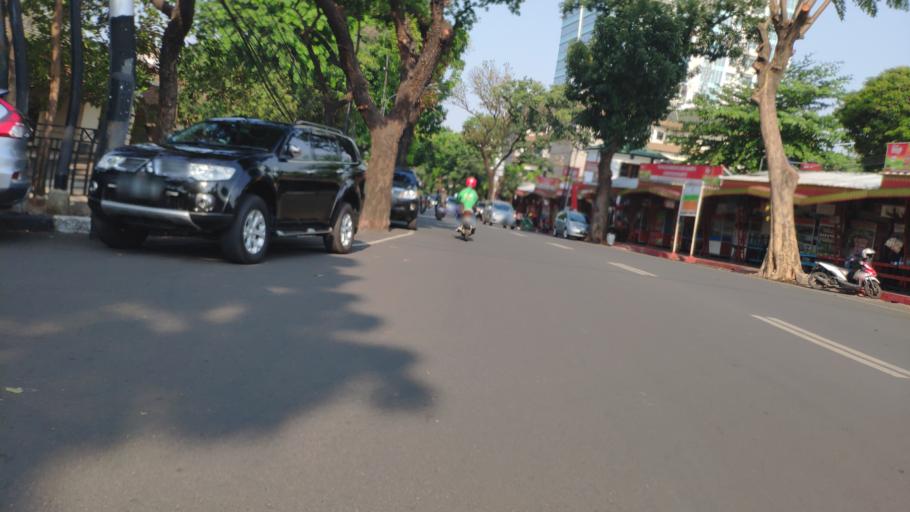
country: ID
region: Jakarta Raya
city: Jakarta
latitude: -6.2465
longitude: 106.7926
